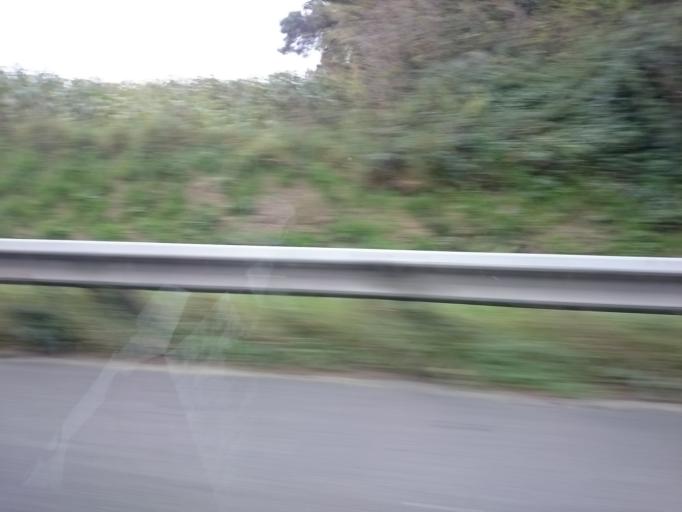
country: FR
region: Brittany
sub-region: Departement des Cotes-d'Armor
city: Coetmieux
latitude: 48.4769
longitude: -2.5996
